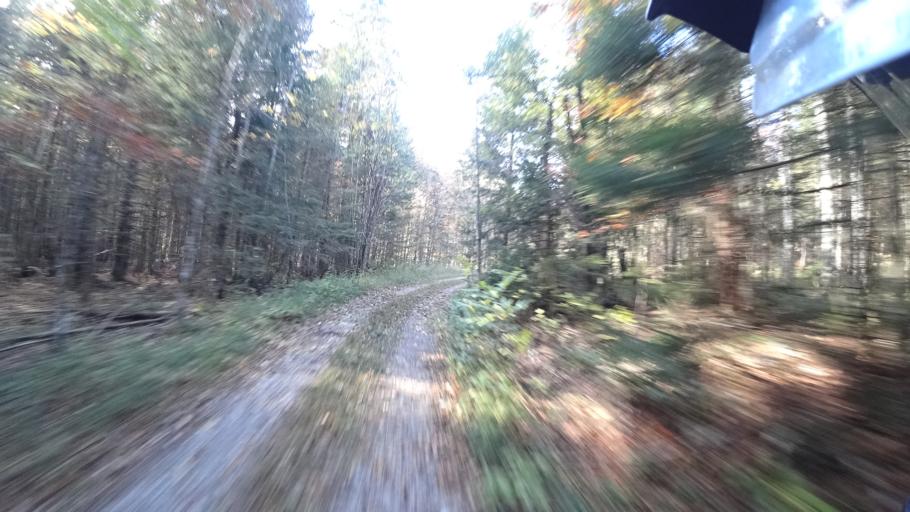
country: HR
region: Karlovacka
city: Plaski
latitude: 45.0462
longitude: 15.3303
